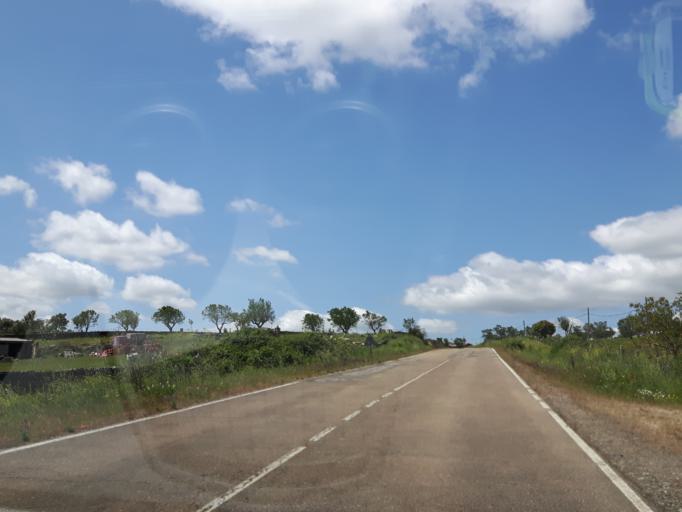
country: ES
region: Castille and Leon
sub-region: Provincia de Salamanca
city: Aldea del Obispo
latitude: 40.7130
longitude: -6.7865
